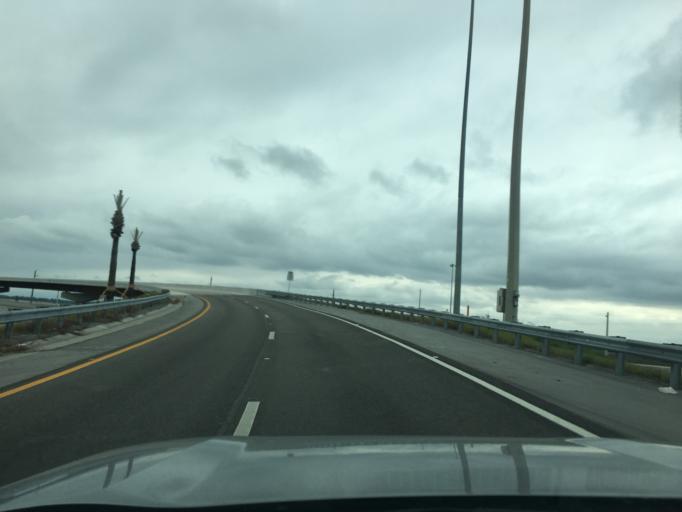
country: US
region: Florida
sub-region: Miami-Dade County
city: Palm Springs North
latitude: 25.9544
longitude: -80.3498
